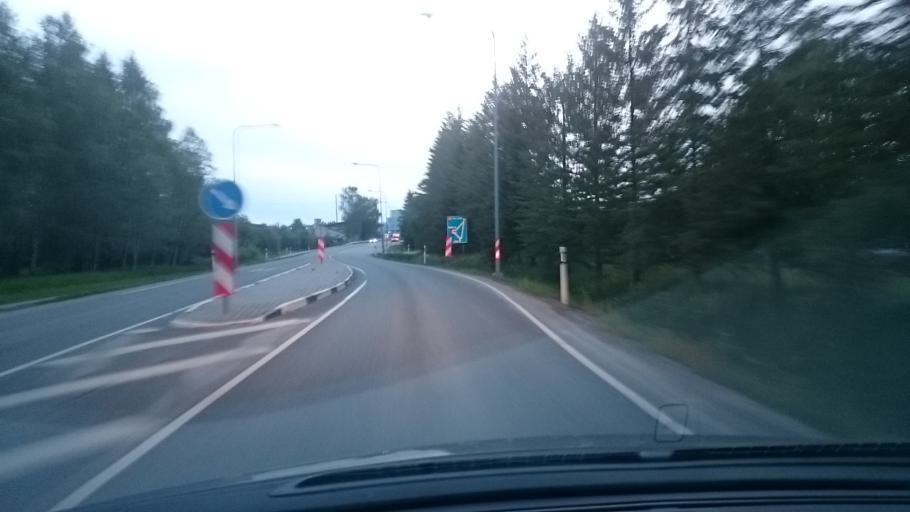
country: EE
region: Raplamaa
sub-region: Rapla vald
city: Rapla
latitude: 58.9880
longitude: 24.8393
